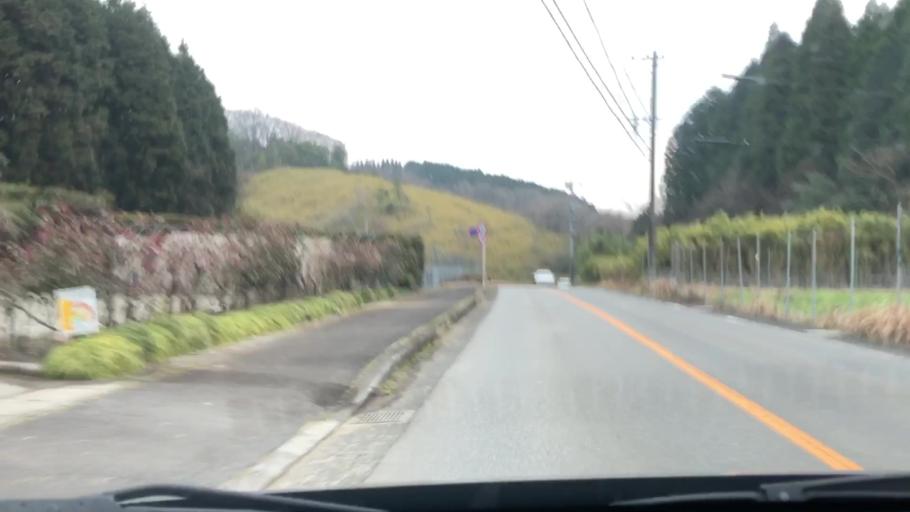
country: JP
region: Oita
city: Usuki
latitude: 33.0050
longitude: 131.6562
